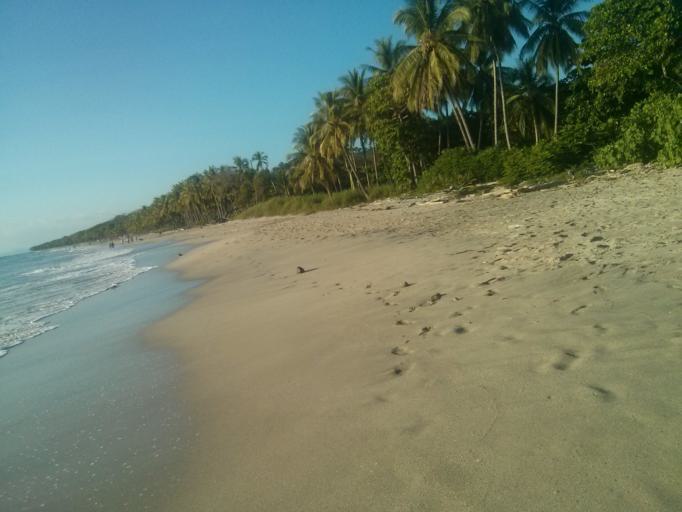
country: CR
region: Guanacaste
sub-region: Canton de Nandayure
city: Bejuco
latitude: 9.6238
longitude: -85.1496
